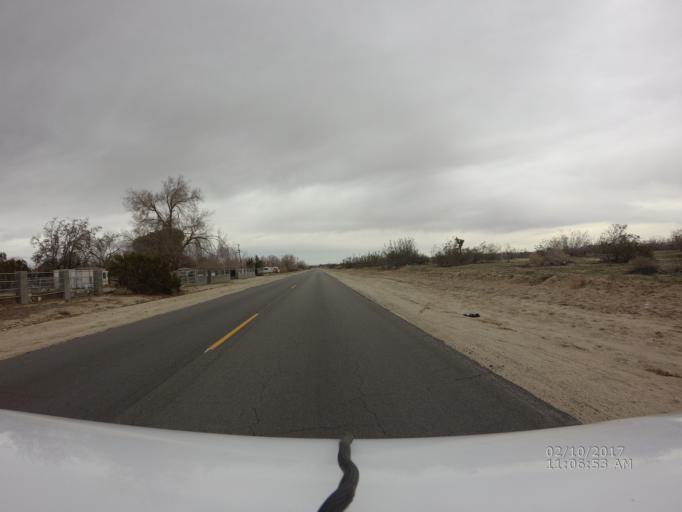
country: US
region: California
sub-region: Los Angeles County
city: Littlerock
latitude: 34.5368
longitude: -117.9581
